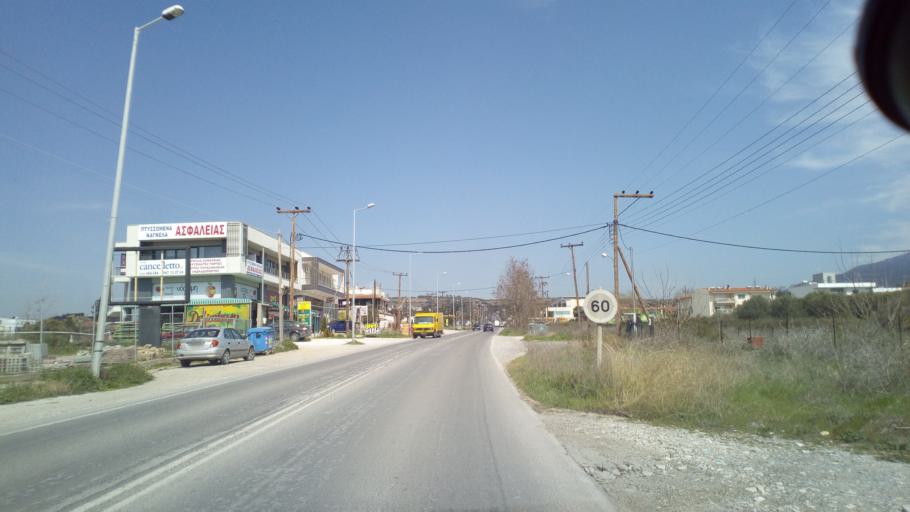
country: GR
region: Central Macedonia
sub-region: Nomos Thessalonikis
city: Thermi
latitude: 40.5563
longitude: 23.0195
